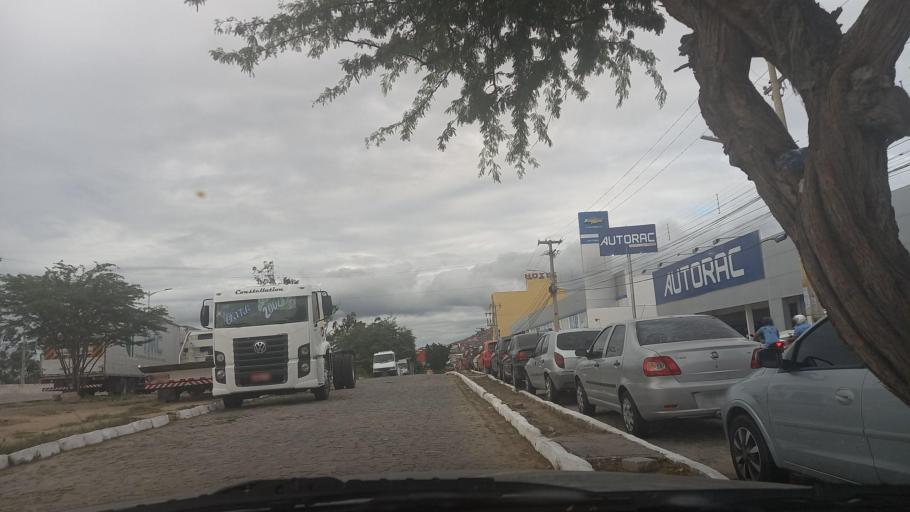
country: BR
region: Pernambuco
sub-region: Caruaru
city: Caruaru
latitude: -8.2963
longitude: -35.9877
